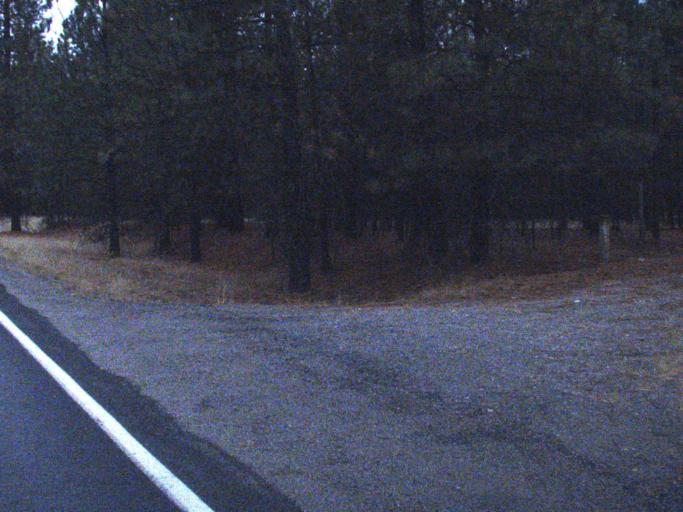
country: US
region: Washington
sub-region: Spokane County
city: Fairchild Air Force Base
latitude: 47.8970
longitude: -117.8227
